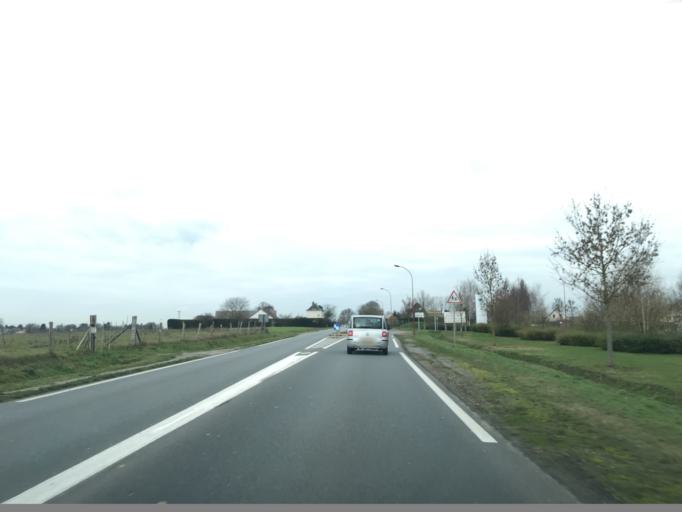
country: FR
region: Haute-Normandie
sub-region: Departement de l'Eure
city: Fleury-sur-Andelle
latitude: 49.3824
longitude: 1.3174
